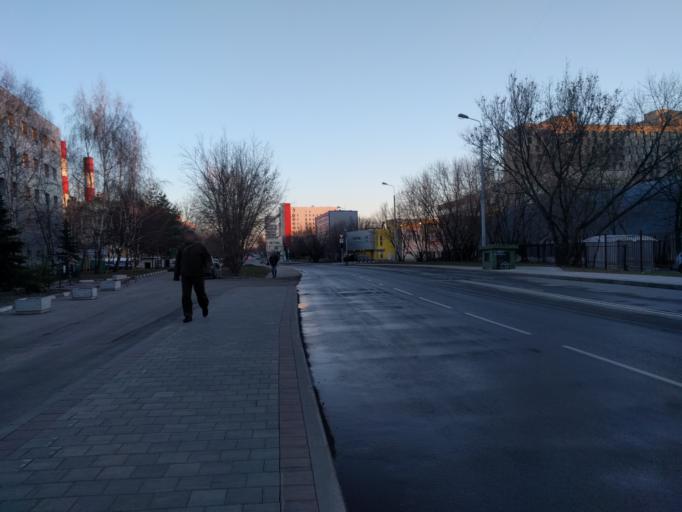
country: RU
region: Moscow
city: Sokol
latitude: 55.7874
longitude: 37.5000
